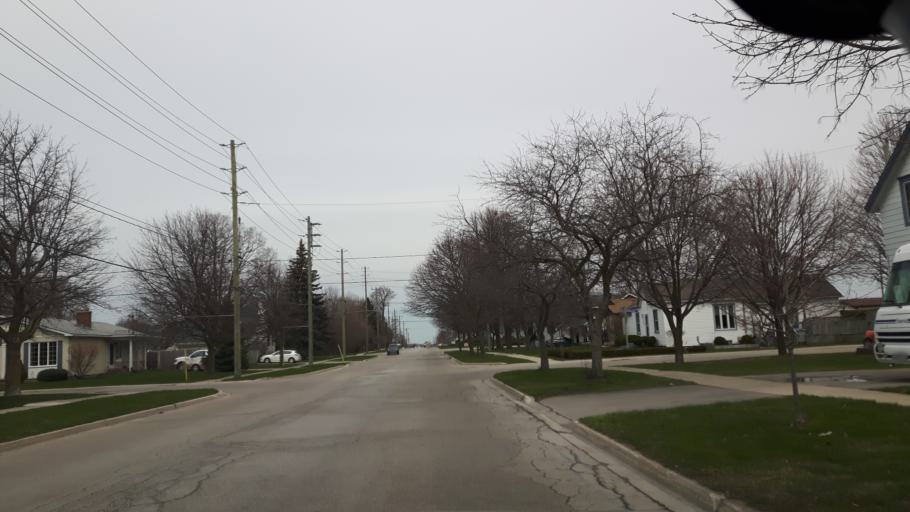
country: CA
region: Ontario
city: Goderich
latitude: 43.7468
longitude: -81.7045
